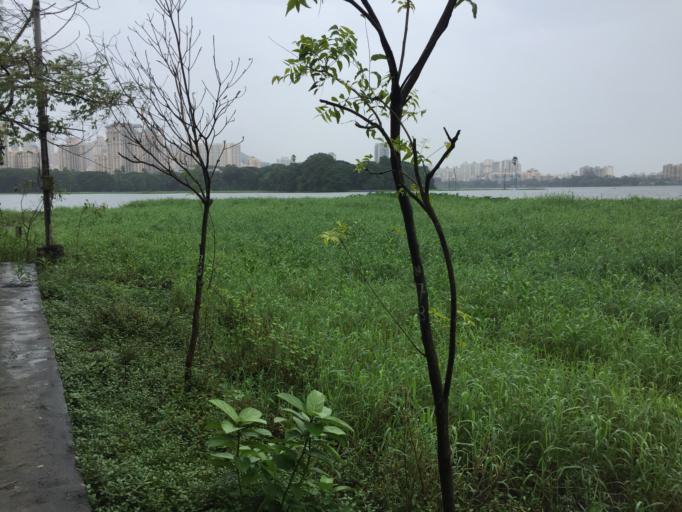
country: IN
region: Maharashtra
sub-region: Mumbai Suburban
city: Powai
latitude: 19.1300
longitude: 72.9103
